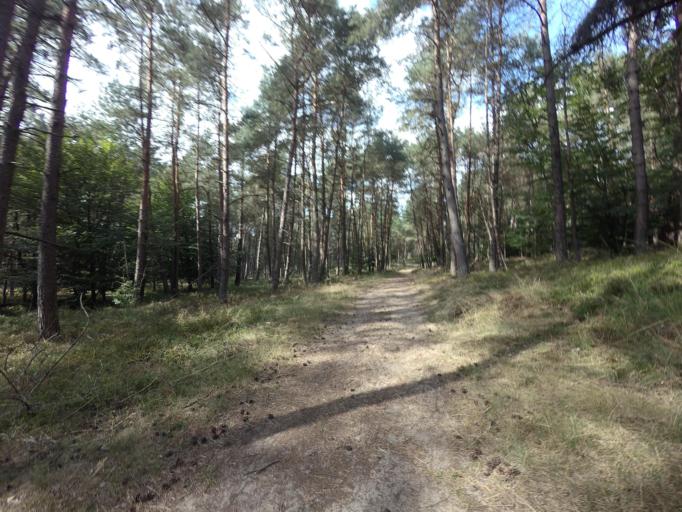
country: NL
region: Gelderland
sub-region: Gemeente Rheden
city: Rheden
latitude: 52.0416
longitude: 6.0270
